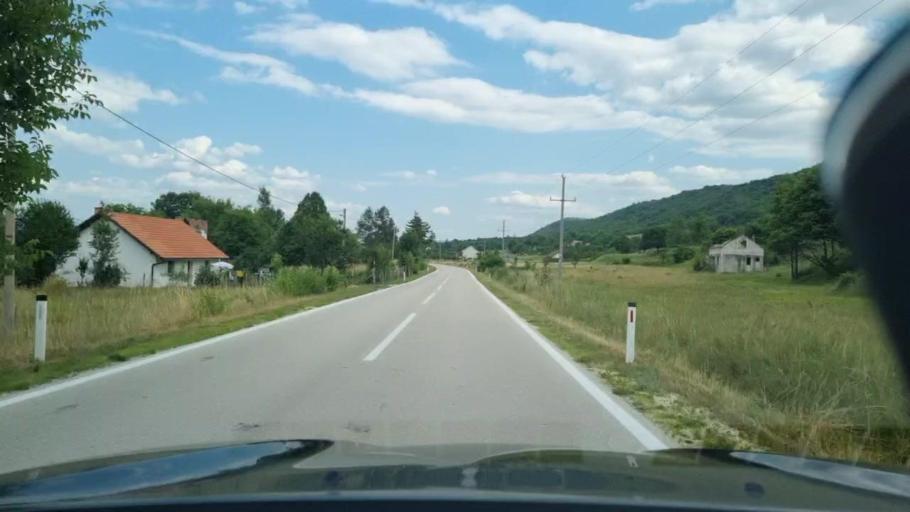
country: HR
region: Splitsko-Dalmatinska
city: Hrvace
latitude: 43.9985
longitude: 16.6111
